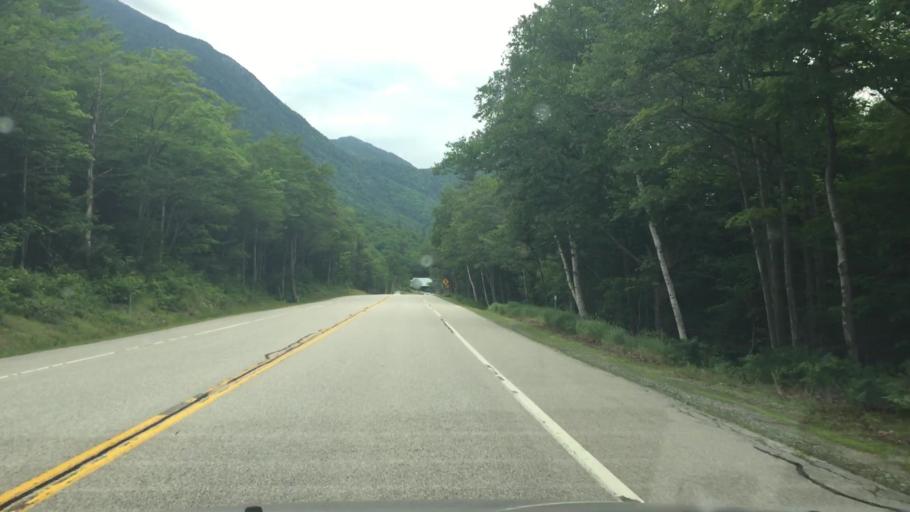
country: US
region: New Hampshire
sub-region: Grafton County
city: Deerfield
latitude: 44.1785
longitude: -71.3959
